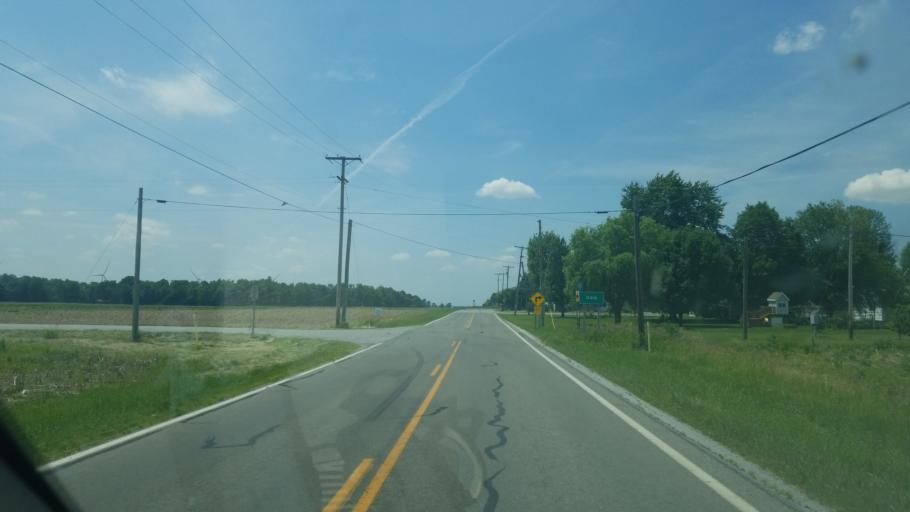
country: US
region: Ohio
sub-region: Hancock County
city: Arlington
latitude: 40.7799
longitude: -83.6897
